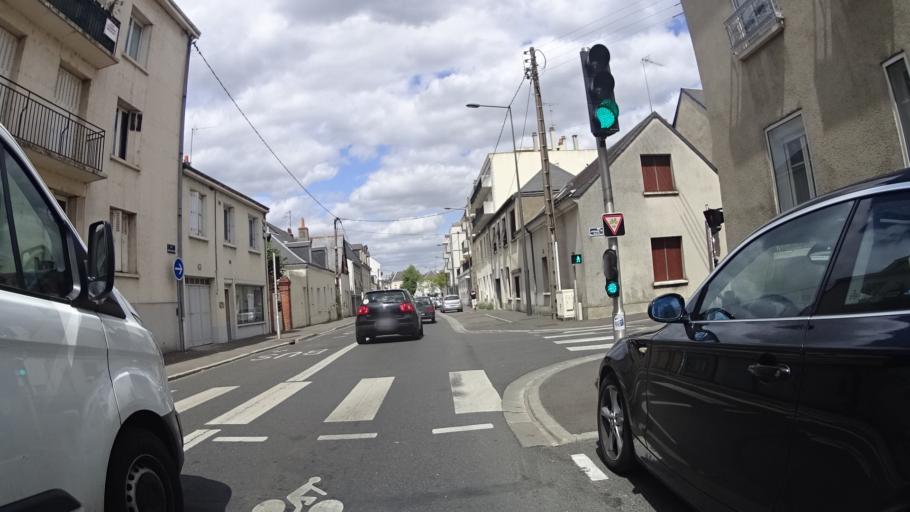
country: FR
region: Centre
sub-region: Departement d'Indre-et-Loire
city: Tours
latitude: 47.3781
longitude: 0.6797
